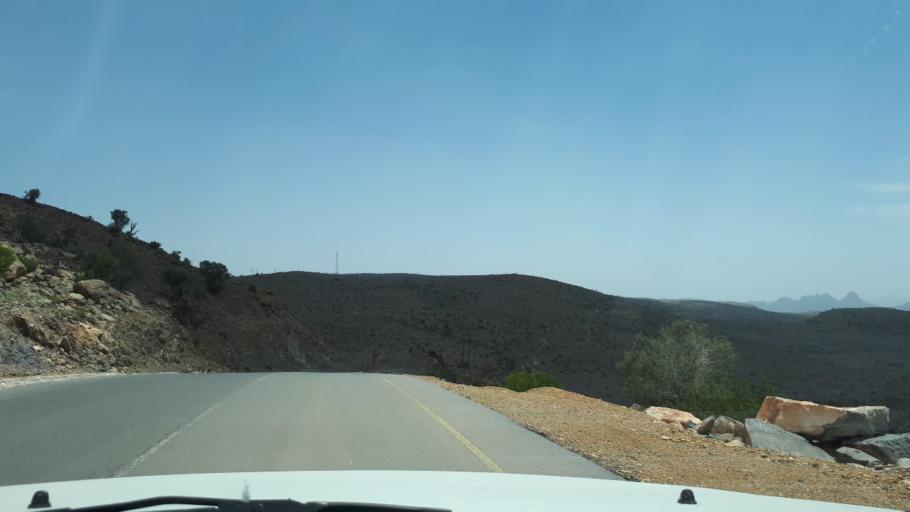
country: OM
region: Al Batinah
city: Rustaq
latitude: 23.2316
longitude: 57.1987
